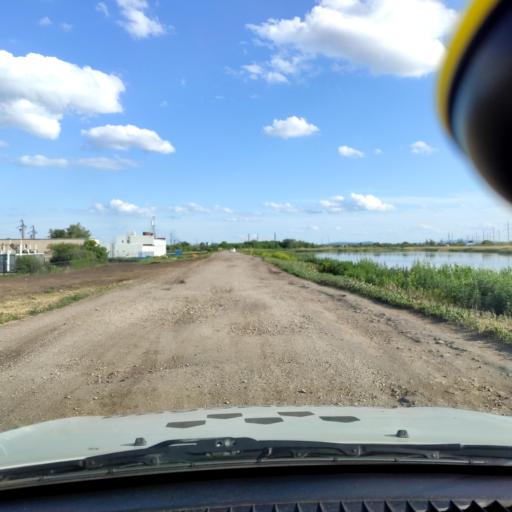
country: RU
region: Samara
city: Tol'yatti
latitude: 53.5941
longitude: 49.4381
